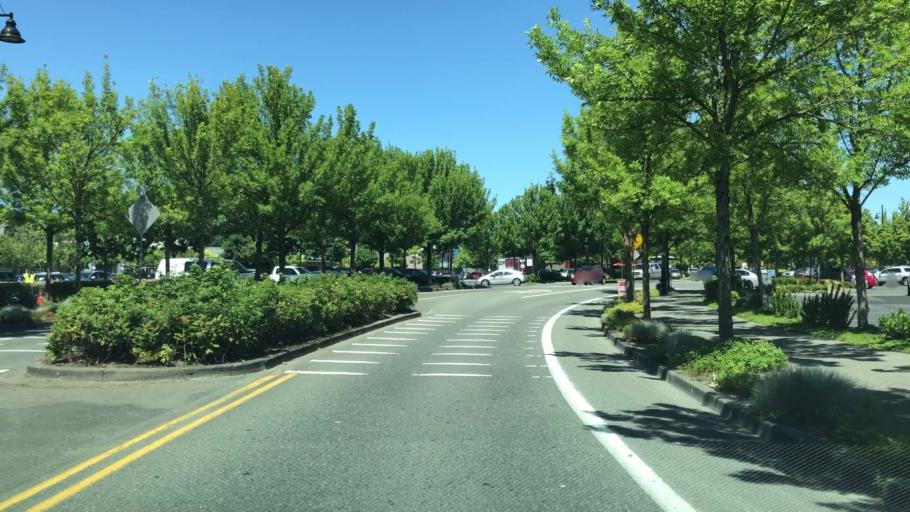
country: US
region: Washington
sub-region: King County
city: Woodinville
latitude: 47.7559
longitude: -122.1555
